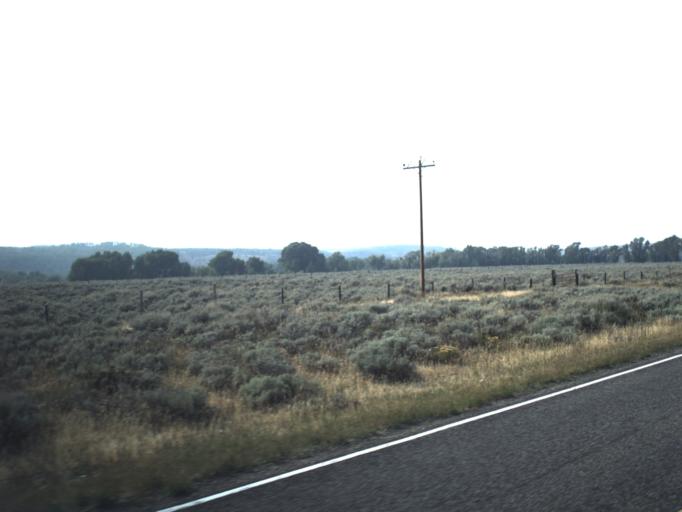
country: US
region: Wyoming
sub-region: Uinta County
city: Evanston
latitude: 40.9886
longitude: -110.8598
